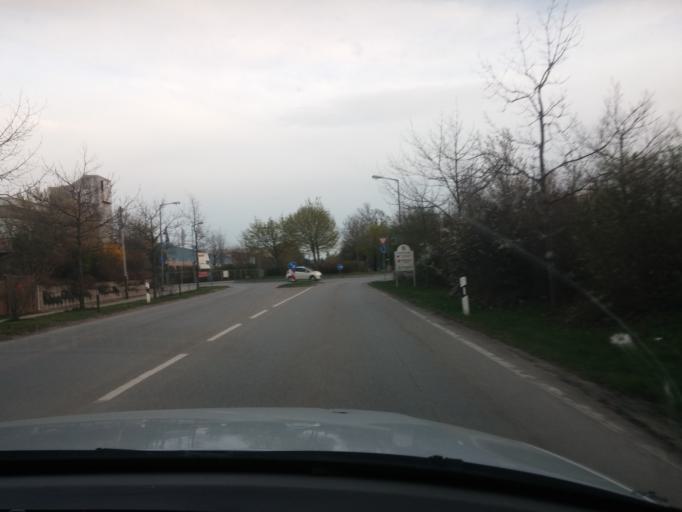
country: DE
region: Bavaria
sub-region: Upper Bavaria
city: Feldkirchen
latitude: 48.1545
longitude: 11.7247
